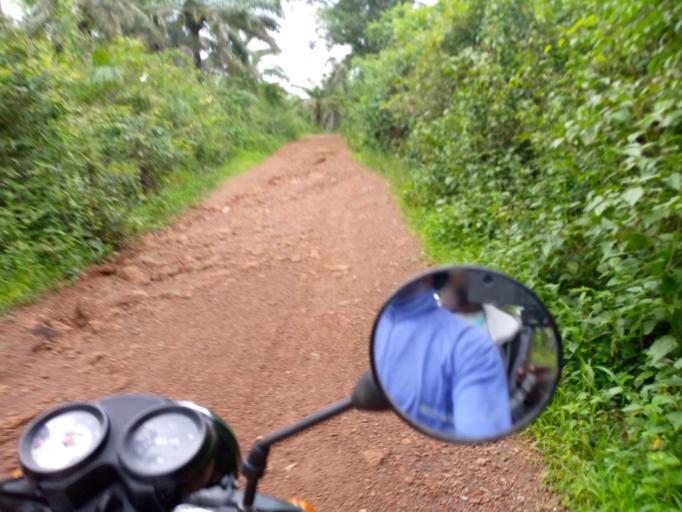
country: SL
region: Northern Province
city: Mange
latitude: 8.9849
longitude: -12.7138
